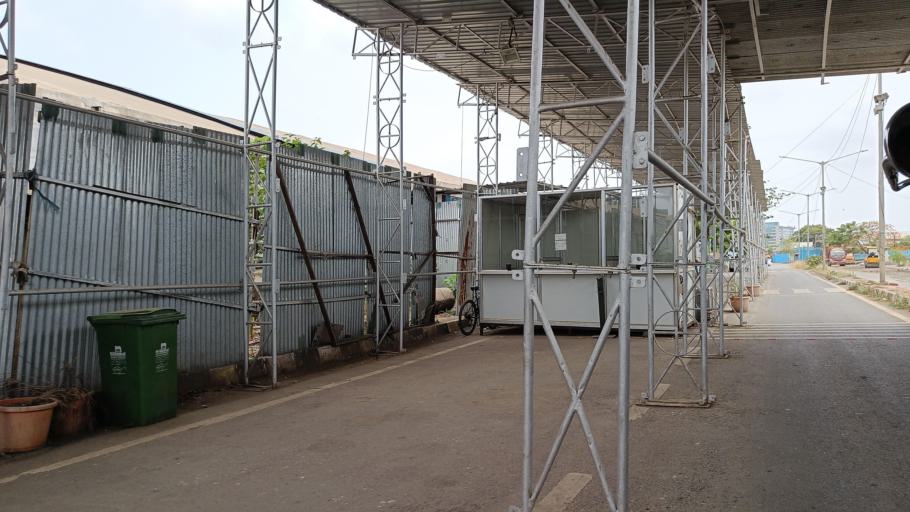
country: IN
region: Maharashtra
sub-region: Mumbai Suburban
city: Mumbai
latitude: 19.0677
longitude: 72.8632
